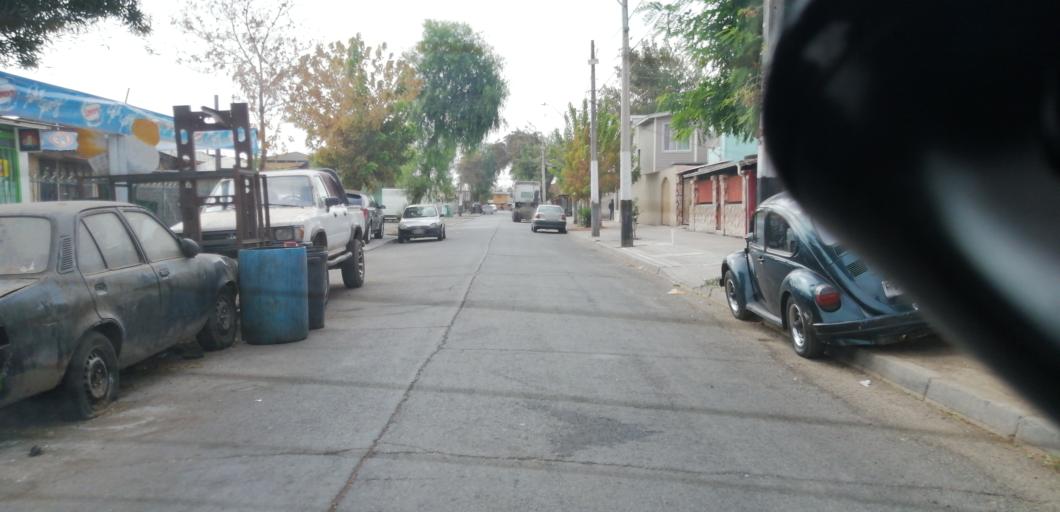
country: CL
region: Santiago Metropolitan
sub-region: Provincia de Santiago
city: Lo Prado
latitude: -33.4354
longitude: -70.7440
